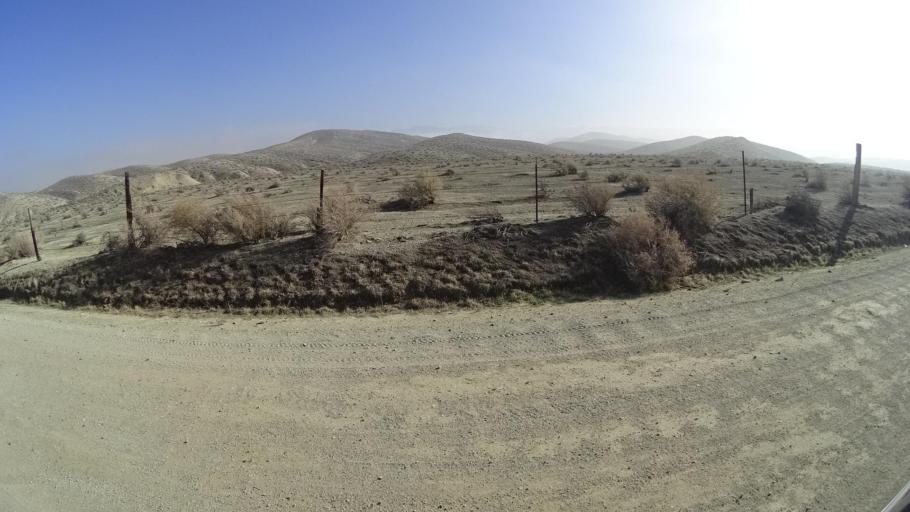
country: US
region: California
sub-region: Kern County
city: Maricopa
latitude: 35.0381
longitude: -119.4328
